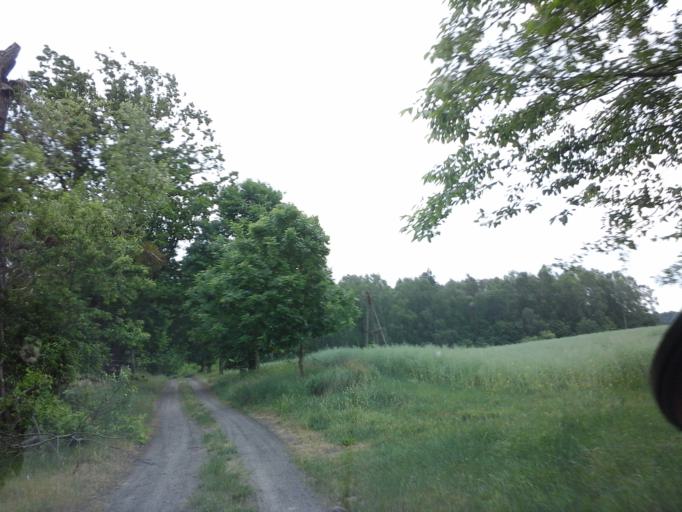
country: PL
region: West Pomeranian Voivodeship
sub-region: Powiat choszczenski
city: Bierzwnik
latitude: 53.1466
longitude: 15.6058
